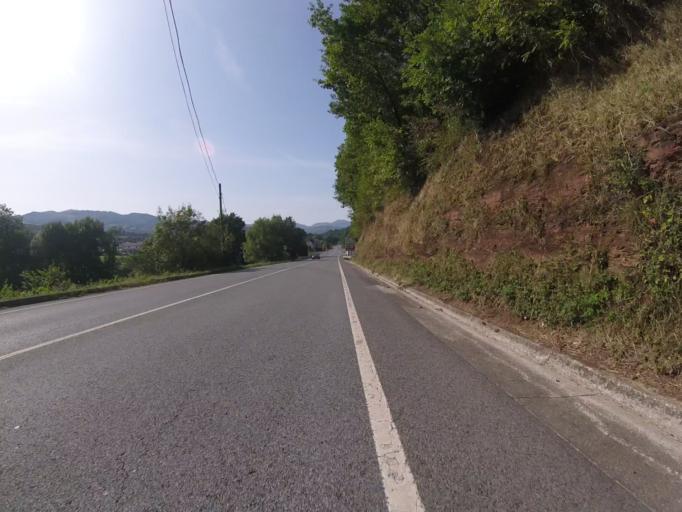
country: ES
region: Navarre
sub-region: Provincia de Navarra
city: Zugarramurdi
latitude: 43.1824
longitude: -1.4896
